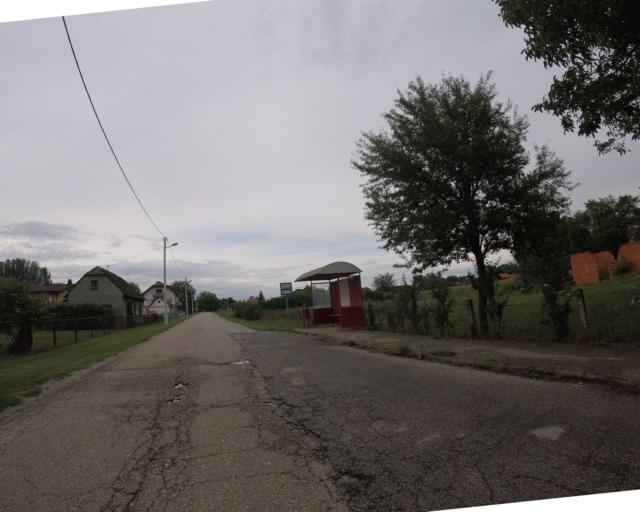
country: HR
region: Zagrebacka
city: Kuce
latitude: 45.7126
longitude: 16.1512
